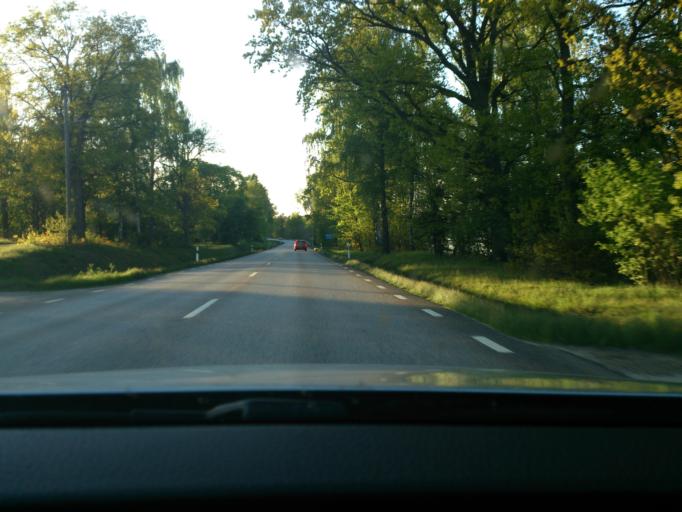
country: SE
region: Kronoberg
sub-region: Vaxjo Kommun
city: Vaexjoe
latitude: 56.9517
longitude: 14.7191
